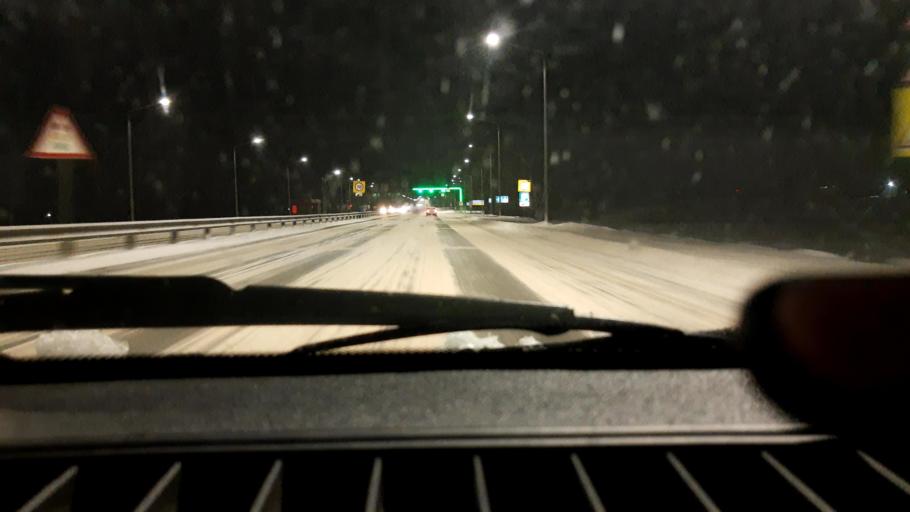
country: RU
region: Bashkortostan
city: Ufa
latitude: 54.5490
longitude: 55.9195
